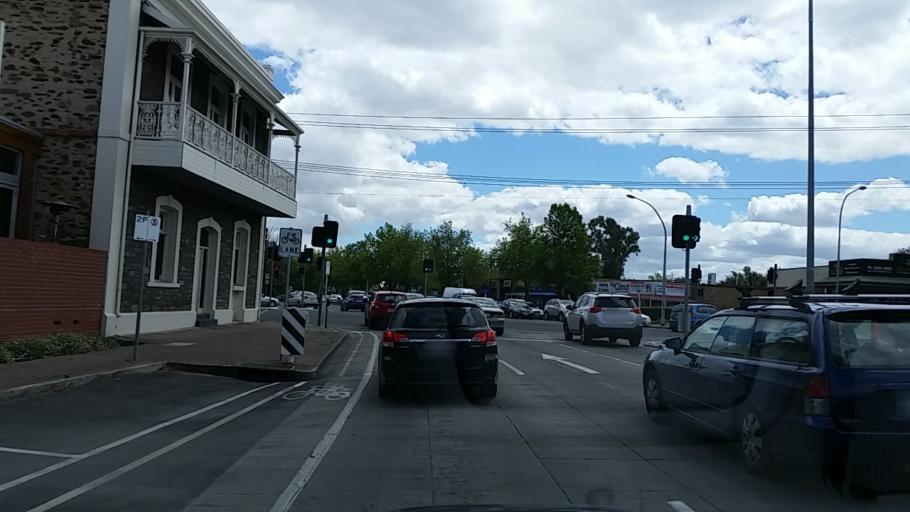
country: AU
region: South Australia
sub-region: Norwood Payneham St Peters
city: Trinity Gardens
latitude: -34.9156
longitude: 138.6316
